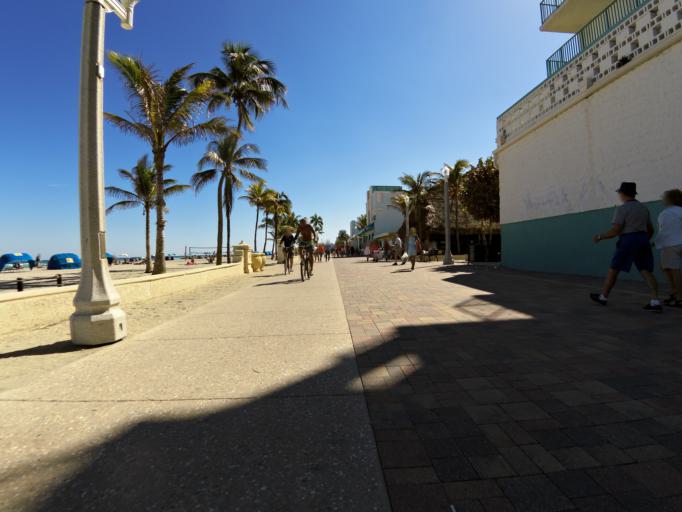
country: US
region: Florida
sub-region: Broward County
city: Hollywood
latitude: 26.0148
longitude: -80.1155
